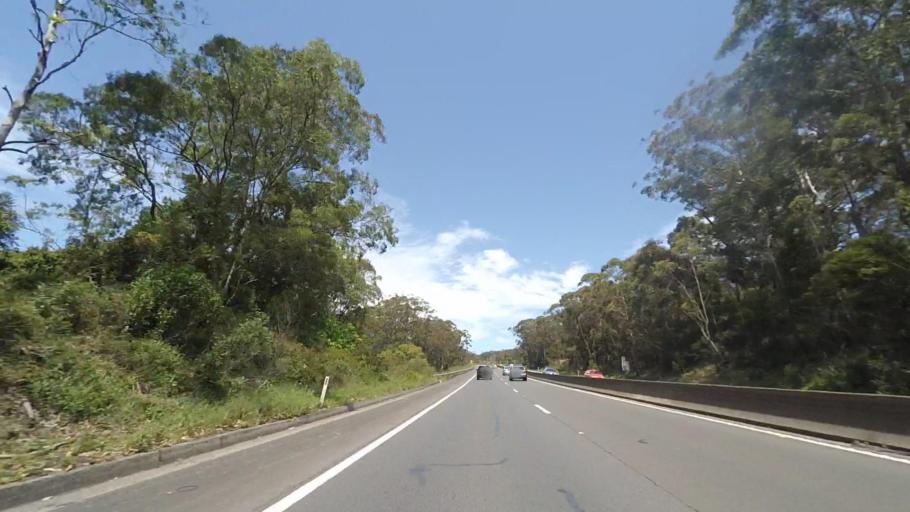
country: AU
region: New South Wales
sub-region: Wollongong
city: Corrimal
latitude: -34.3521
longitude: 150.8660
